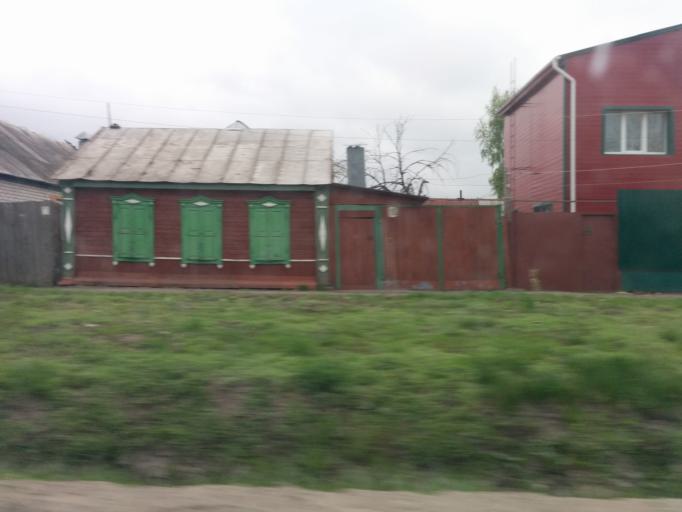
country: RU
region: Tambov
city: Tambov
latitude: 52.7334
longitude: 41.4346
